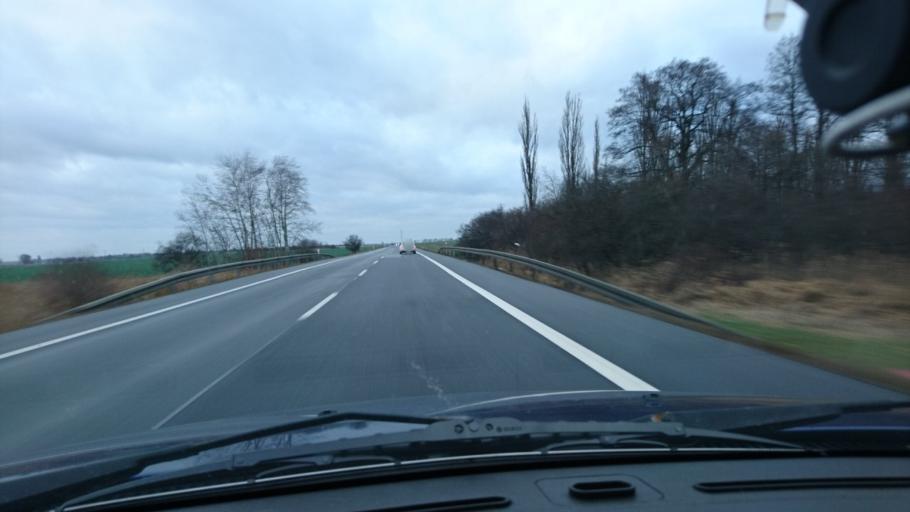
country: PL
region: Opole Voivodeship
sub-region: Powiat kluczborski
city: Kluczbork
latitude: 50.9848
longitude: 18.2409
